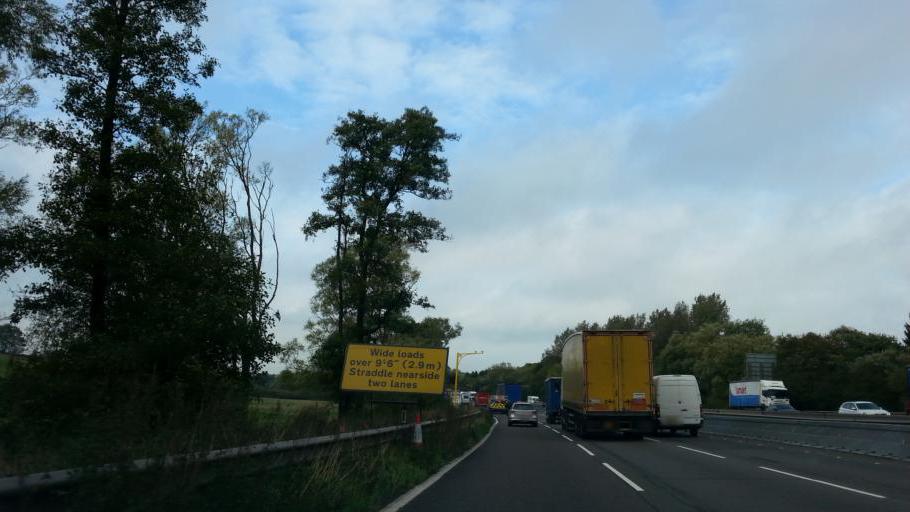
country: GB
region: England
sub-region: Staffordshire
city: Newcastle under Lyme
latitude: 52.9780
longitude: -2.2285
